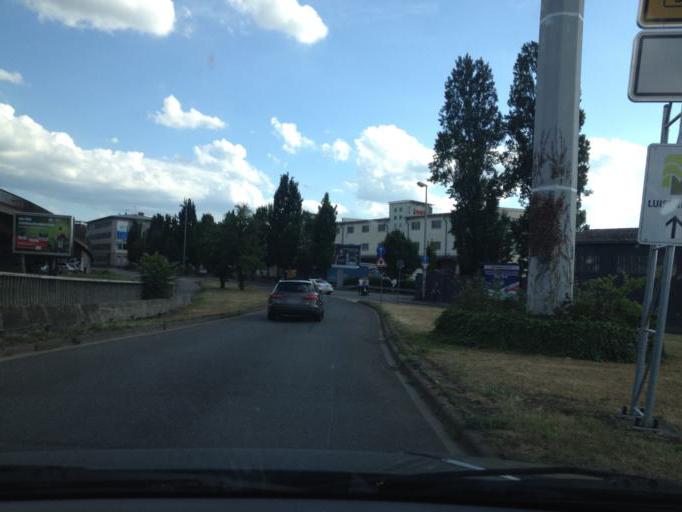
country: DE
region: Rheinland-Pfalz
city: Ludwigshafen am Rhein
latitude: 49.4904
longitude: 8.4568
